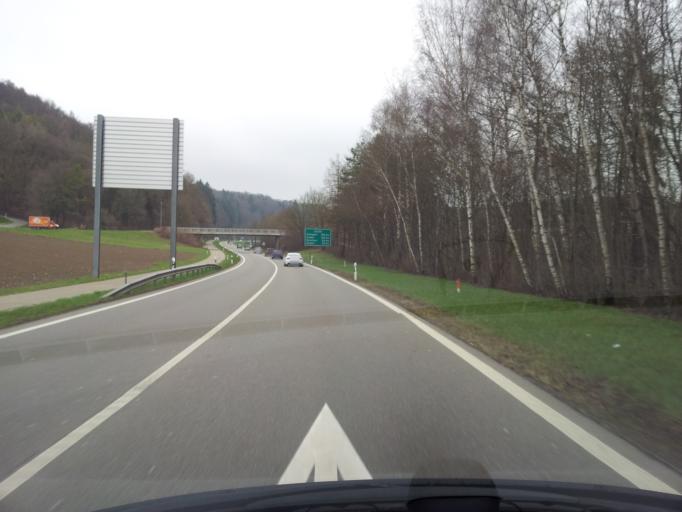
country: CH
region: Schaffhausen
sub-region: Bezirk Reiat
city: Stetten
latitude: 47.7210
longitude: 8.6681
